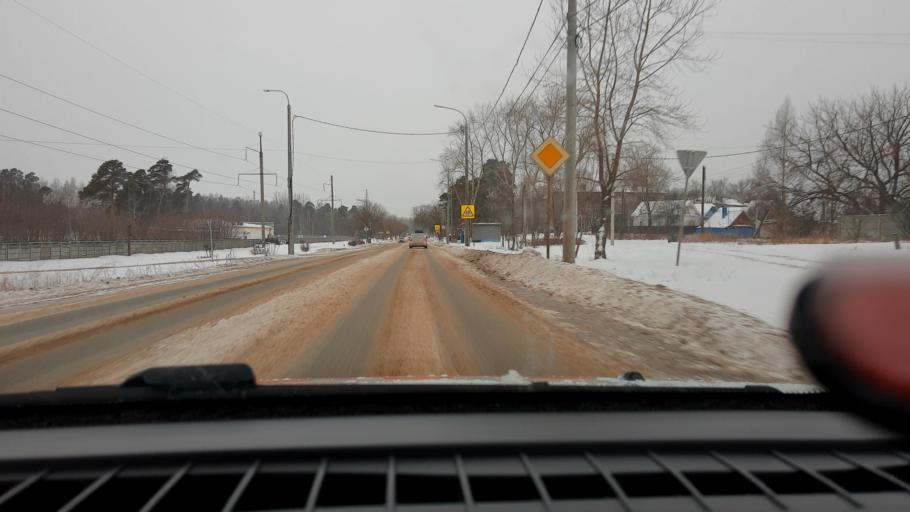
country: RU
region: Nizjnij Novgorod
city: Bor
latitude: 56.3300
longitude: 44.1203
